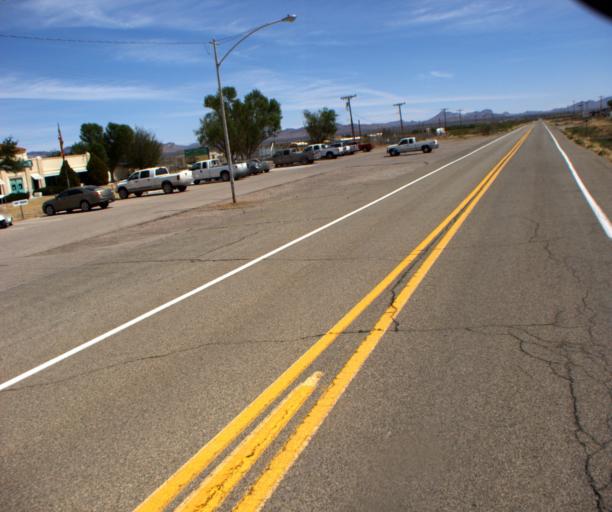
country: US
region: New Mexico
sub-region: Hidalgo County
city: Lordsburg
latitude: 32.2658
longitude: -109.2241
